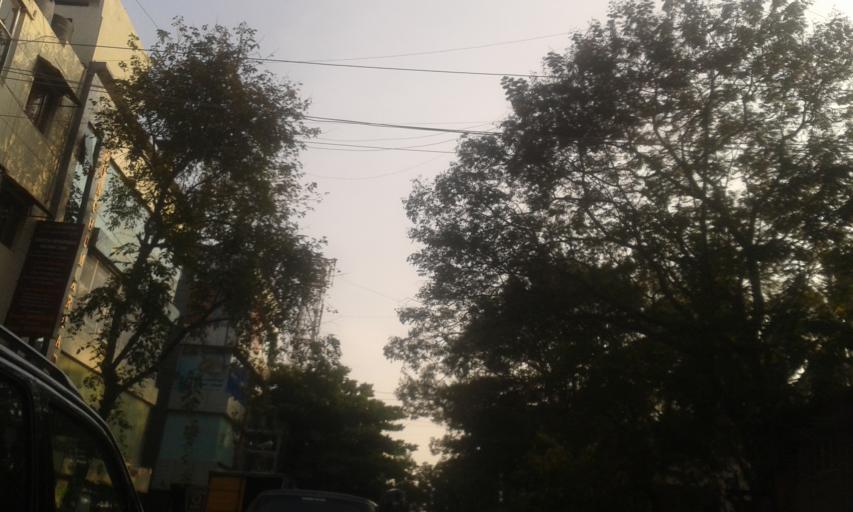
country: IN
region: Karnataka
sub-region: Bangalore Urban
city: Bangalore
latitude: 12.9159
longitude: 77.5950
